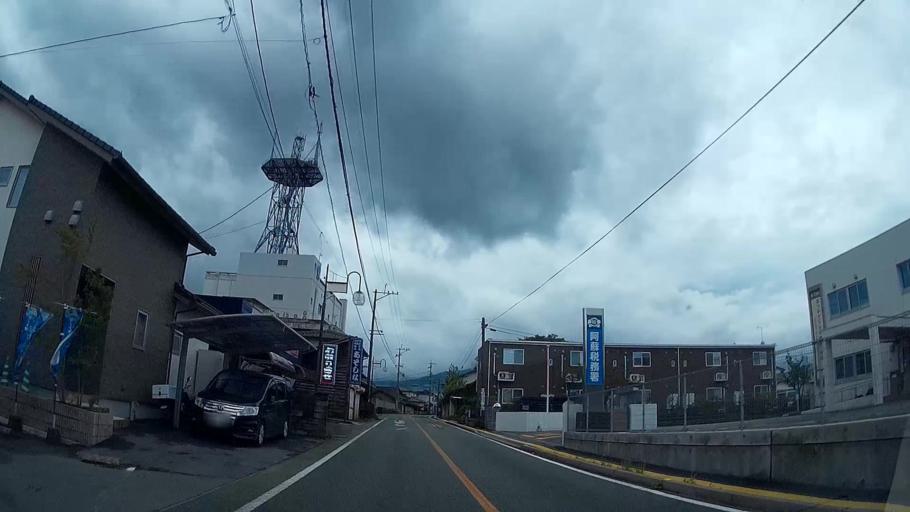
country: JP
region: Kumamoto
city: Aso
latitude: 32.9470
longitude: 131.1178
